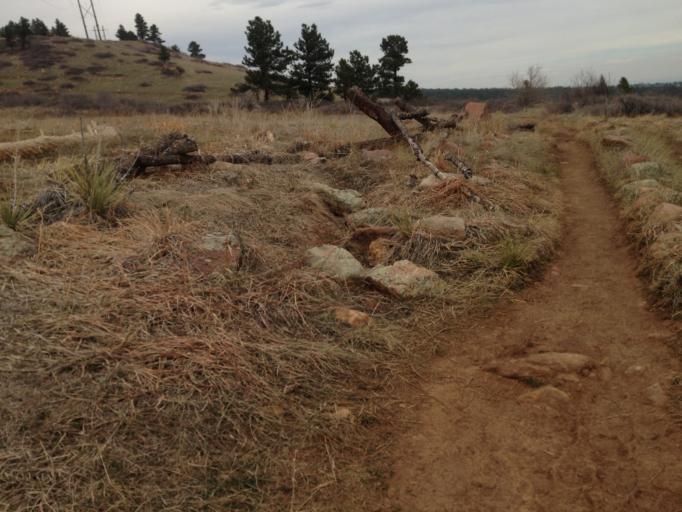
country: US
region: Colorado
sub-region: Boulder County
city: Boulder
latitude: 39.9487
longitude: -105.2675
